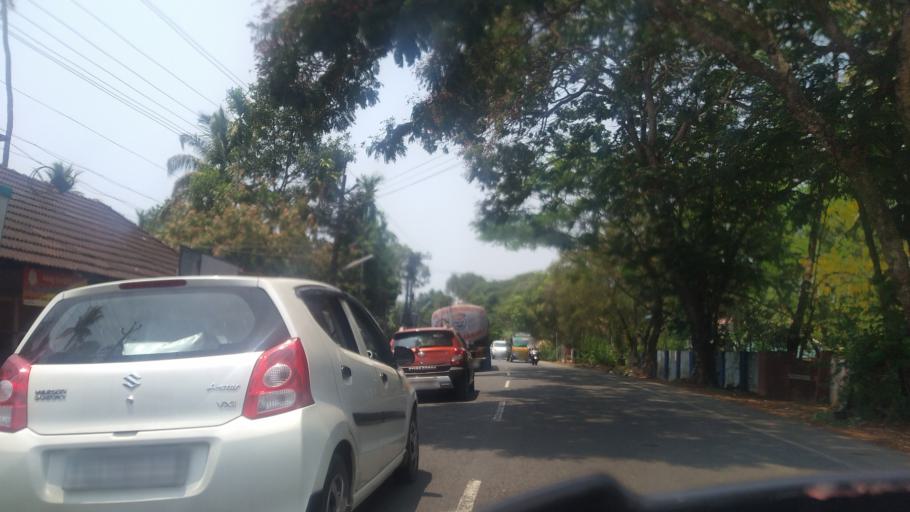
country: IN
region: Kerala
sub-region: Thrissur District
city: Kodungallur
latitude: 10.2709
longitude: 76.1769
